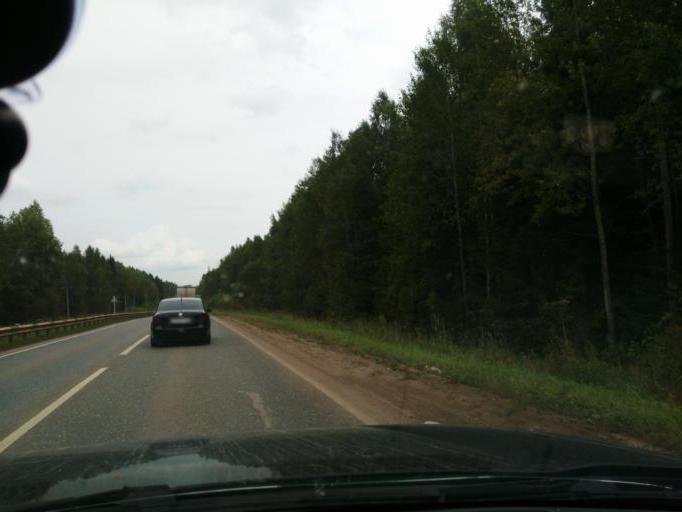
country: RU
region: Bashkortostan
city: Verkhniye Tatyshly
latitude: 56.4979
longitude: 55.8393
